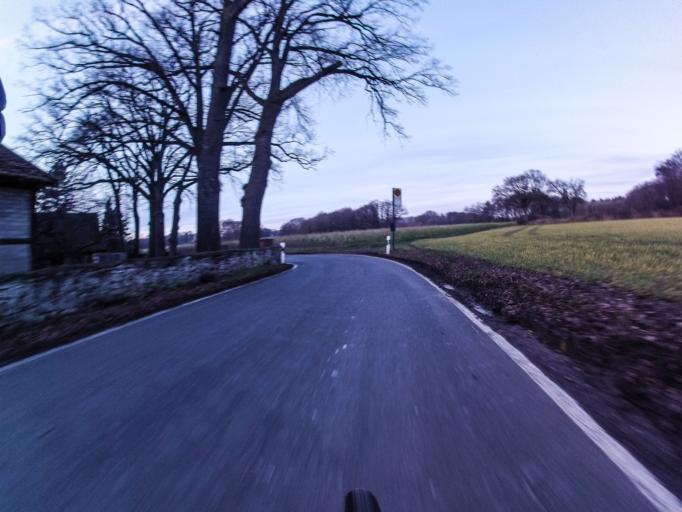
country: DE
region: North Rhine-Westphalia
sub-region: Regierungsbezirk Munster
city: Tecklenburg
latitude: 52.2607
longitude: 7.8081
